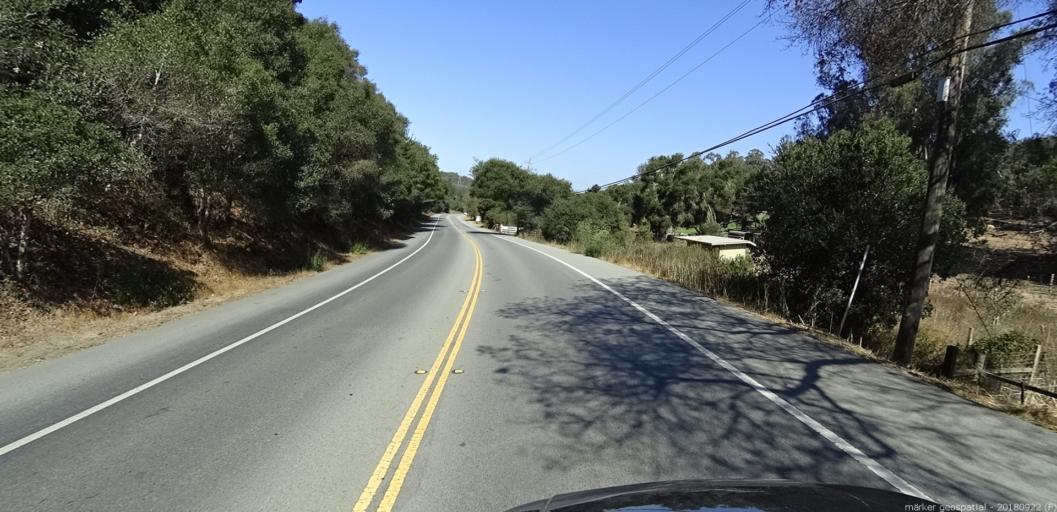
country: US
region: California
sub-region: Monterey County
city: Las Lomas
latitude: 36.8388
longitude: -121.6843
